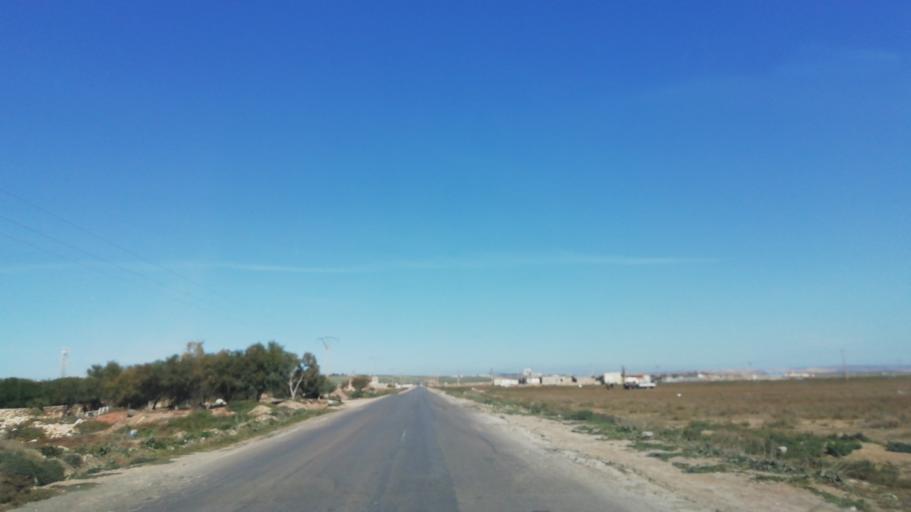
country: DZ
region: Oran
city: Es Senia
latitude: 35.5175
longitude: -0.5888
